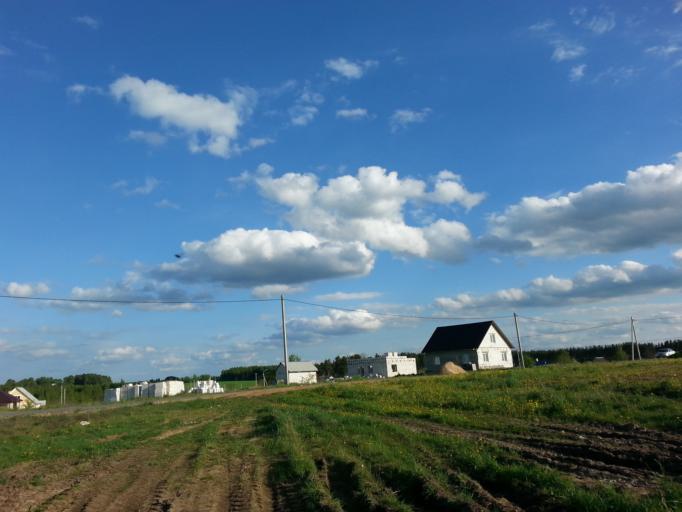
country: BY
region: Minsk
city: Narach
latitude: 54.9372
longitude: 26.7014
